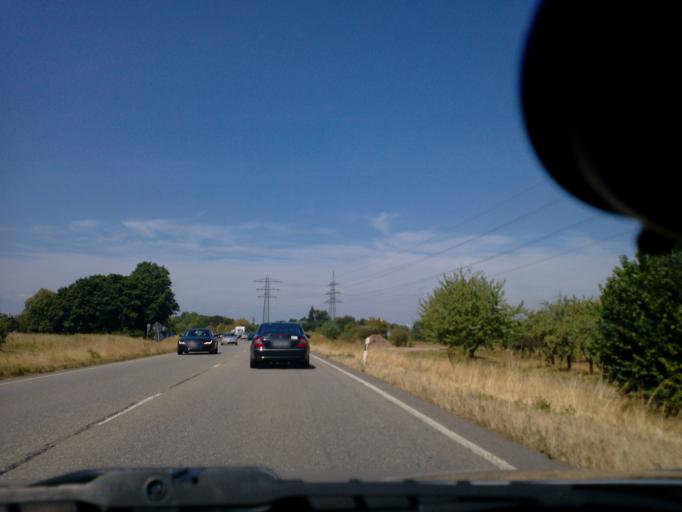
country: DE
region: Baden-Wuerttemberg
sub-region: Freiburg Region
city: Ortenberg
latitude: 48.4463
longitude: 7.9492
